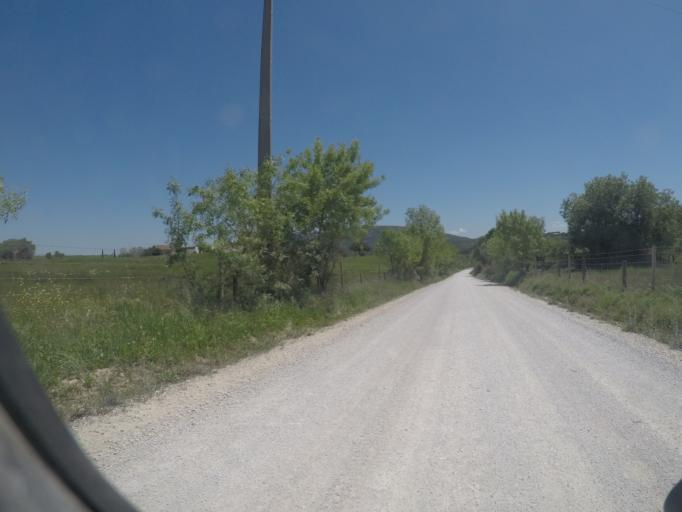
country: PT
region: Setubal
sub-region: Sesimbra
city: Sesimbra
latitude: 38.4616
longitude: -9.0610
